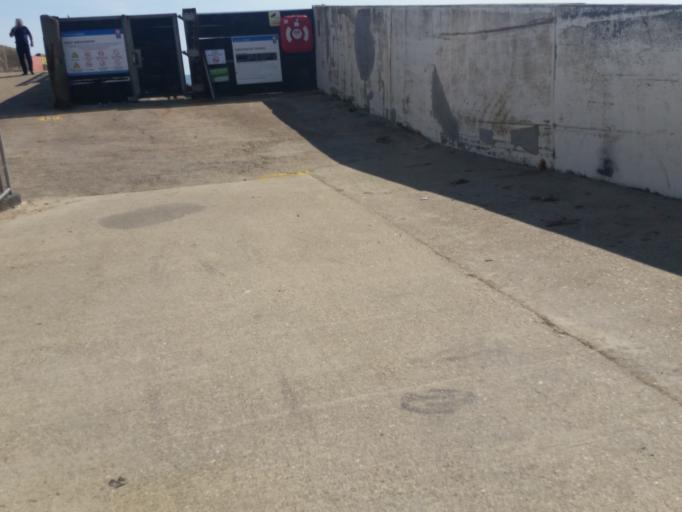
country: GB
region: England
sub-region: Brighton and Hove
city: Brighton
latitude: 50.8123
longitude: -0.1076
